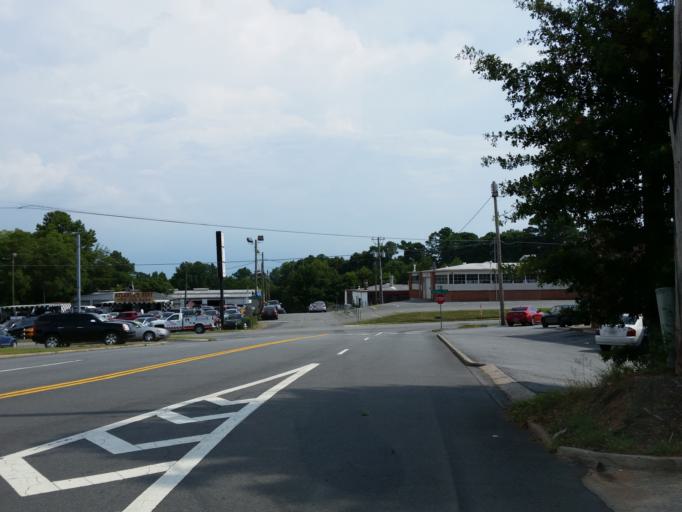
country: US
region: Georgia
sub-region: Cobb County
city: Marietta
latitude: 33.9516
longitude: -84.5256
